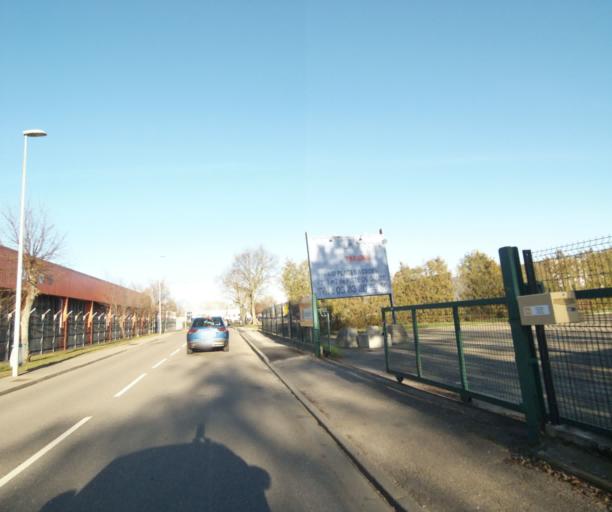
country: FR
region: Lorraine
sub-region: Departement de Meurthe-et-Moselle
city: Pulnoy
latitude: 48.7077
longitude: 6.2467
